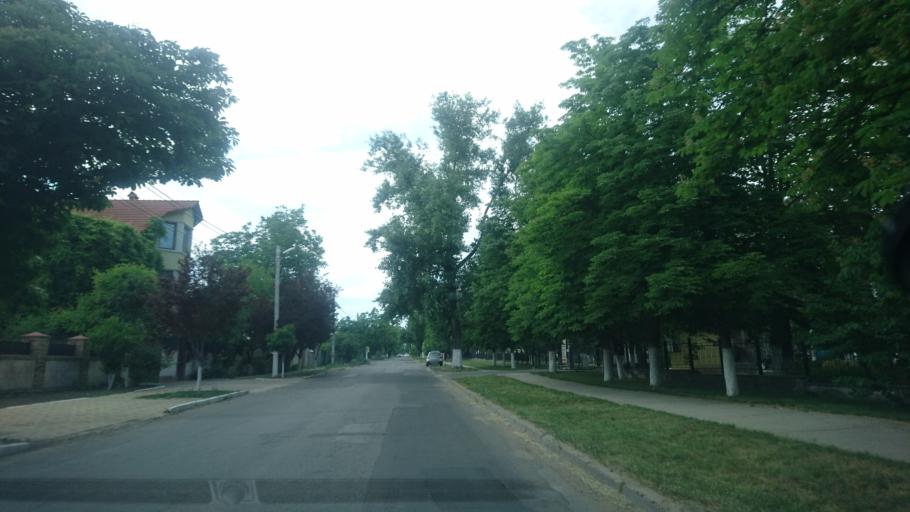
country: MD
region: Chisinau
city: Stauceni
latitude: 47.0581
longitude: 28.8389
